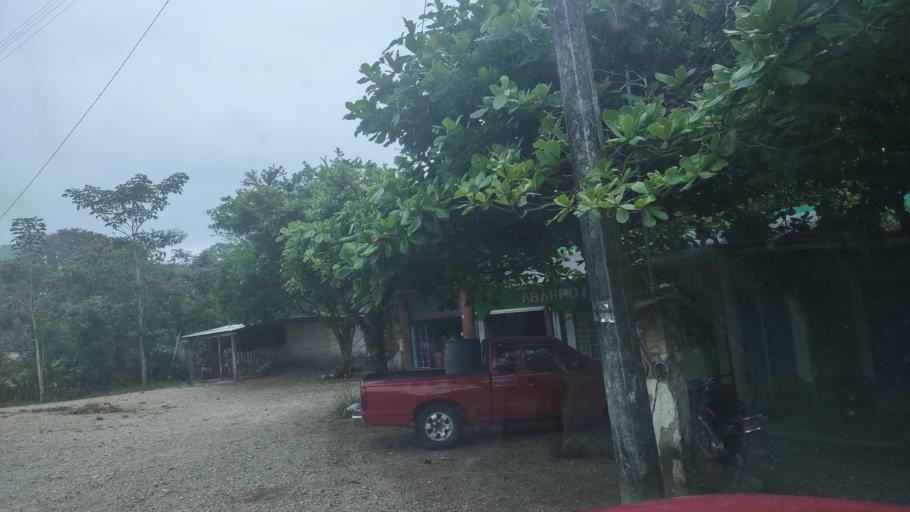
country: MX
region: Veracruz
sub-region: Uxpanapa
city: Poblado 10
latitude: 17.4744
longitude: -94.1213
